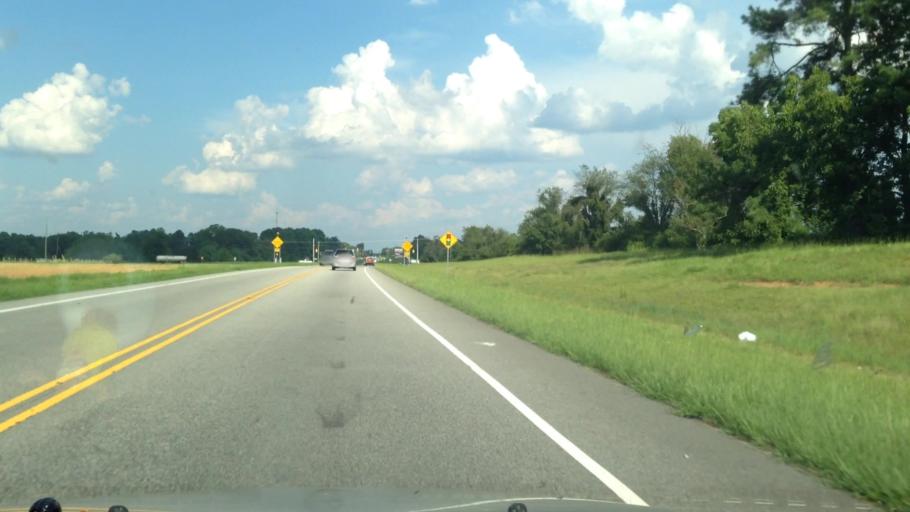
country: US
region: North Carolina
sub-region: Lee County
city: Broadway
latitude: 35.4388
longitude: -79.0405
